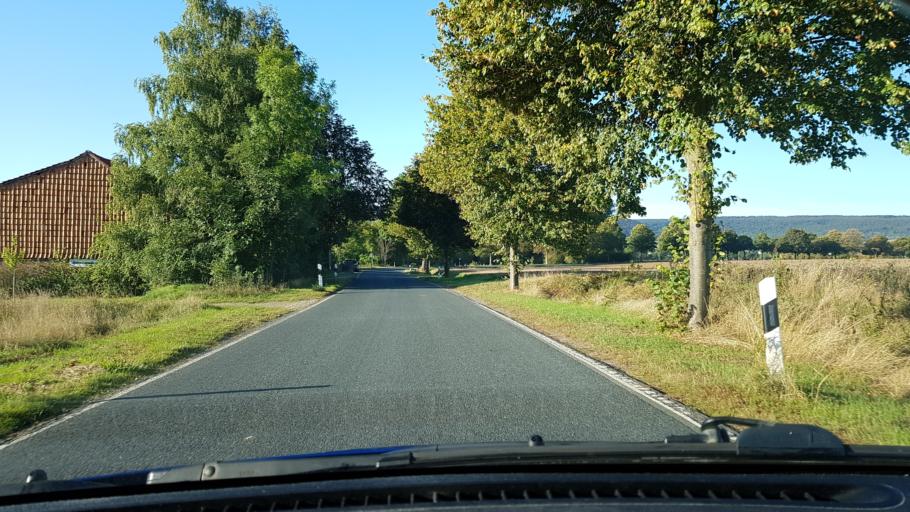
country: DE
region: Lower Saxony
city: Bad Munder am Deister
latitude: 52.2149
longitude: 9.4248
